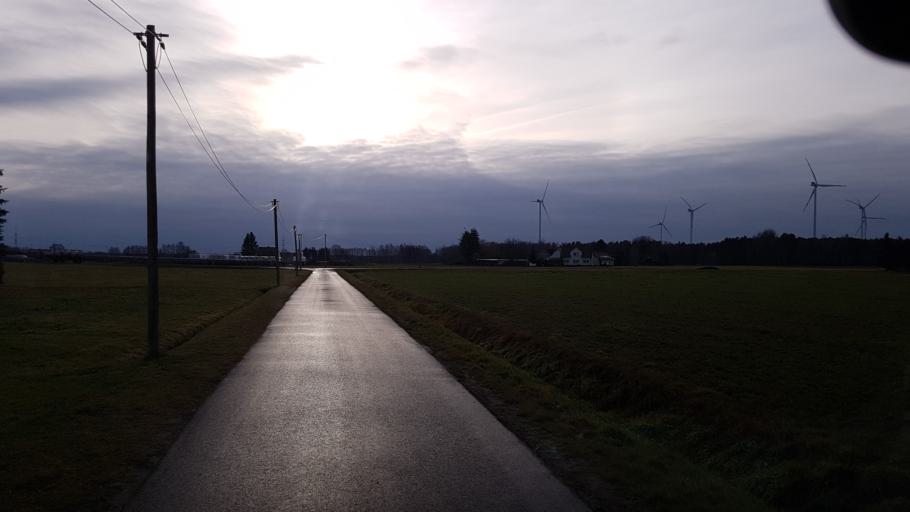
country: DE
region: Brandenburg
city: Sallgast
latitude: 51.6411
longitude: 13.8521
